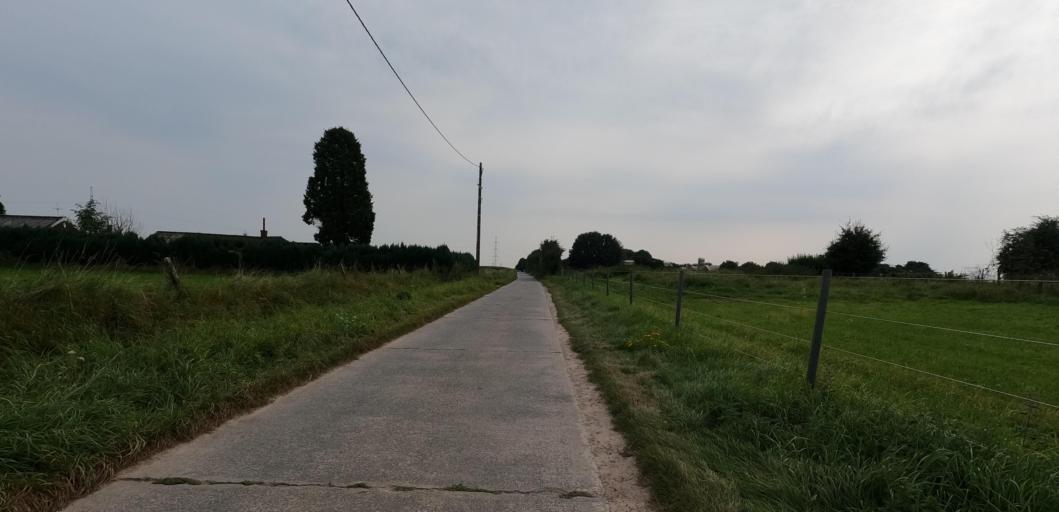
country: BE
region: Flanders
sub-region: Provincie Vlaams-Brabant
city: Merchtem
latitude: 50.9797
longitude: 4.2332
